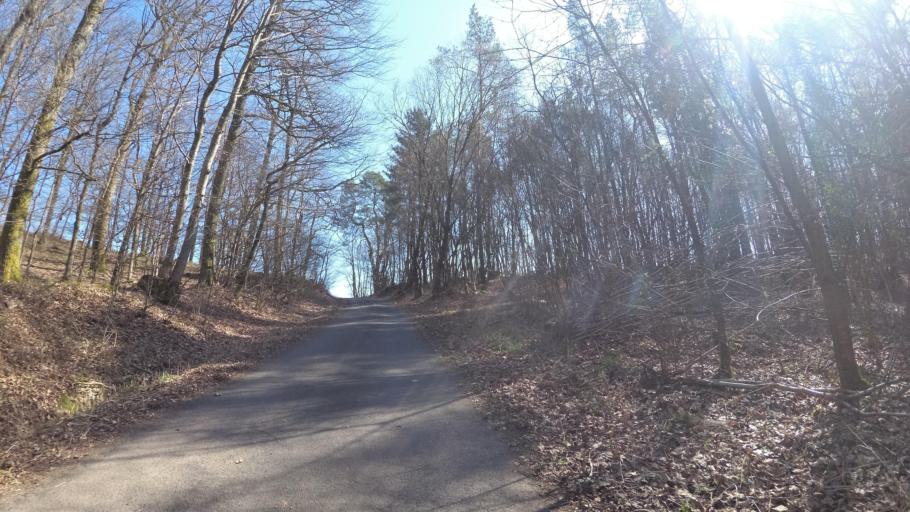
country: DE
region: Rheinland-Pfalz
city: Dambach
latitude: 49.6329
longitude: 7.1264
